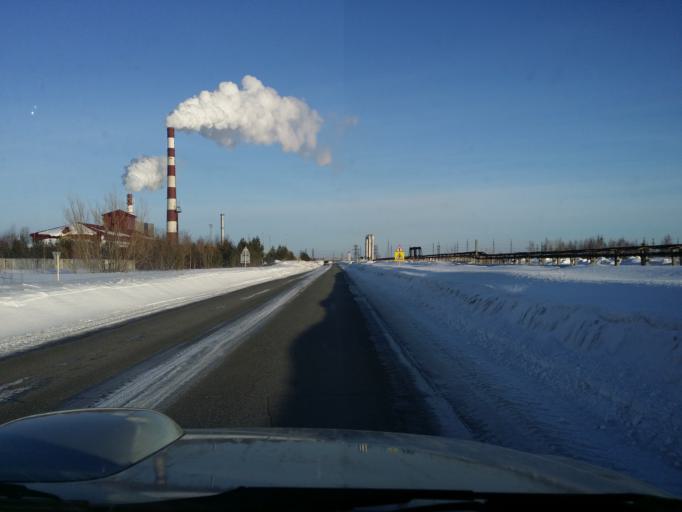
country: RU
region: Khanty-Mansiyskiy Avtonomnyy Okrug
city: Izluchinsk
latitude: 60.9790
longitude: 76.9197
